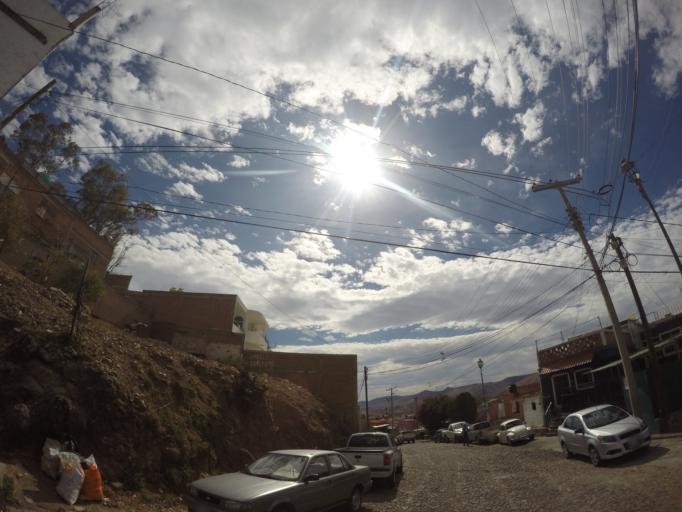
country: MX
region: Guanajuato
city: Guanajuato
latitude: 21.0158
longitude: -101.2594
